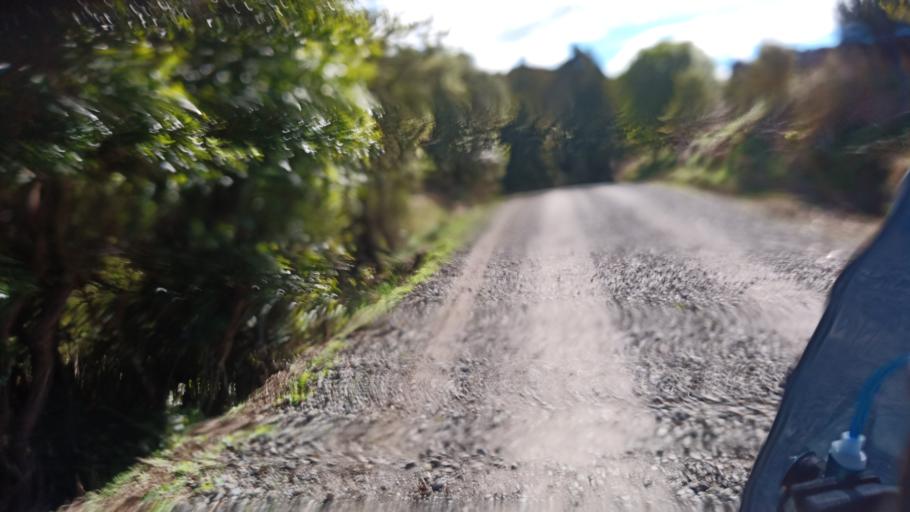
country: NZ
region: Hawke's Bay
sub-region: Wairoa District
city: Wairoa
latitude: -38.8192
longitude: 177.1608
